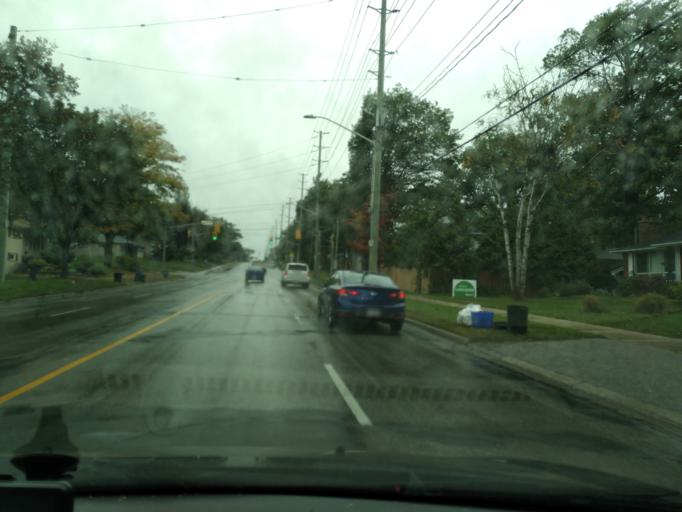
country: CA
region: Ontario
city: Barrie
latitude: 44.3911
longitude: -79.7126
